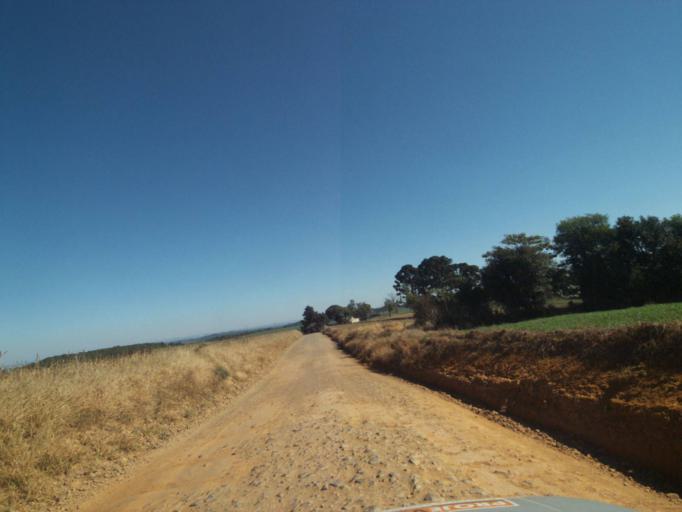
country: BR
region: Parana
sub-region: Tibagi
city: Tibagi
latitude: -24.6199
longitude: -50.6121
